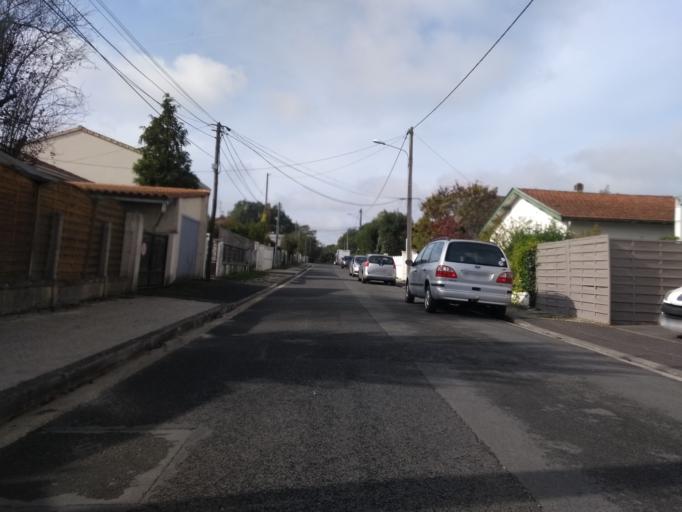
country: FR
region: Aquitaine
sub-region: Departement de la Gironde
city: Pessac
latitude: 44.7972
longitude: -0.6326
